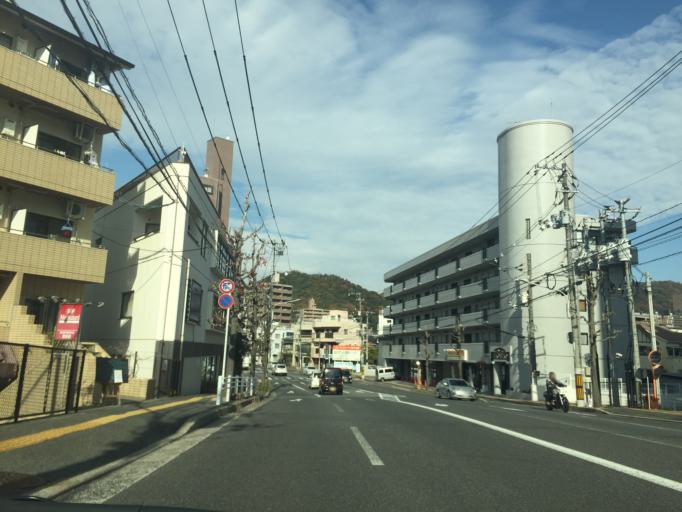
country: JP
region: Hiroshima
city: Hiroshima-shi
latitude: 34.4081
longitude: 132.4716
